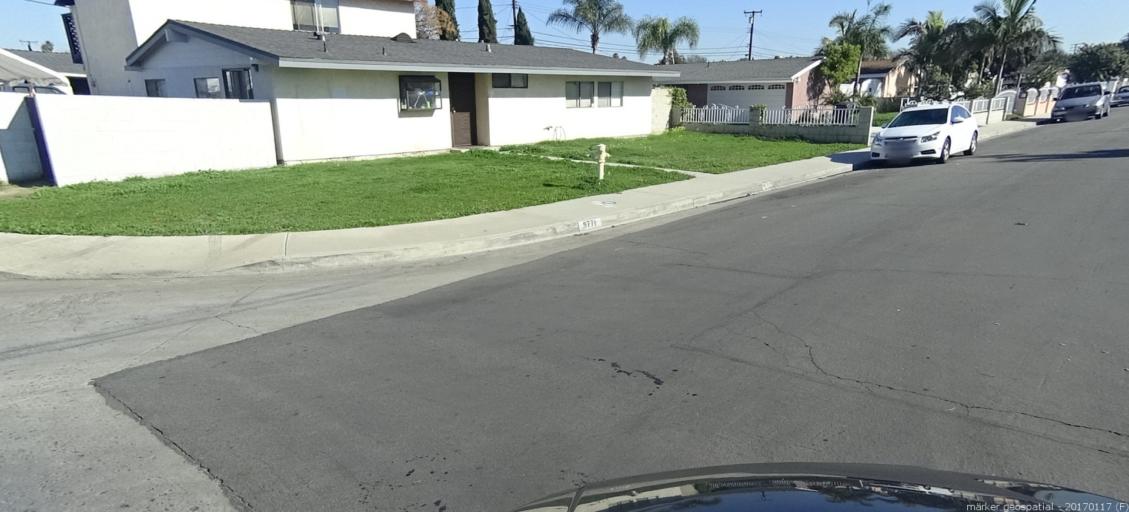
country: US
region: California
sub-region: Orange County
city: Stanton
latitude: 33.8119
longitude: -117.9627
